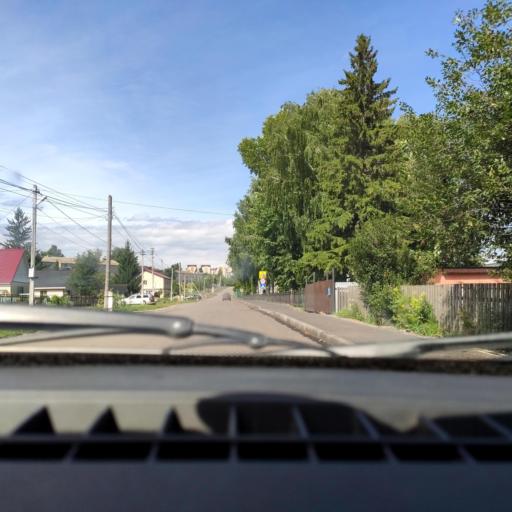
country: RU
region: Bashkortostan
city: Mikhaylovka
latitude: 54.8057
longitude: 55.8935
